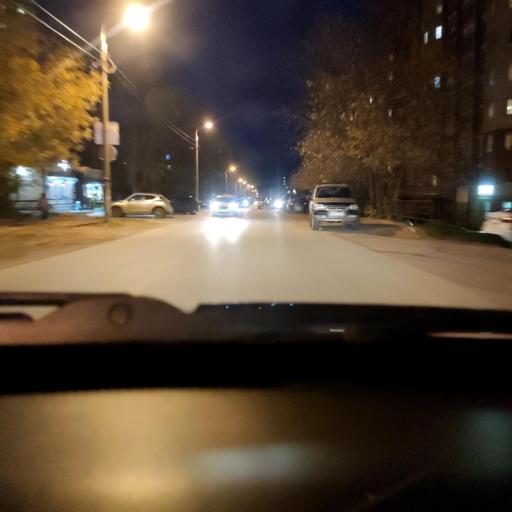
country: RU
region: Perm
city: Perm
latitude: 58.1008
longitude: 56.3019
